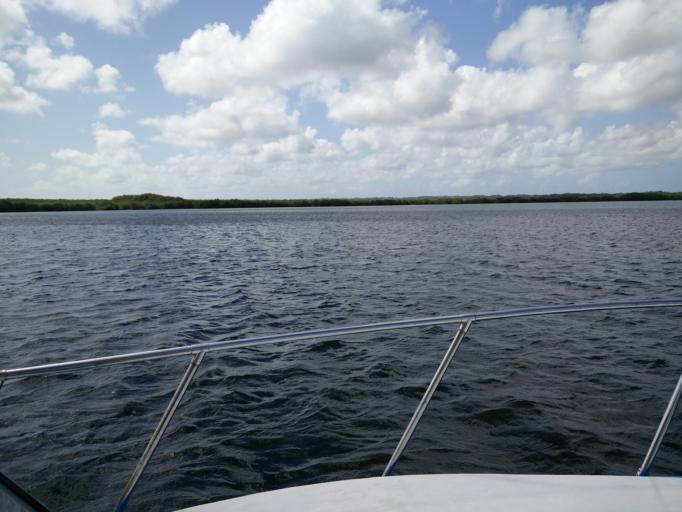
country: GP
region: Guadeloupe
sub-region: Guadeloupe
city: Petit-Canal
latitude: 16.3723
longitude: -61.4999
